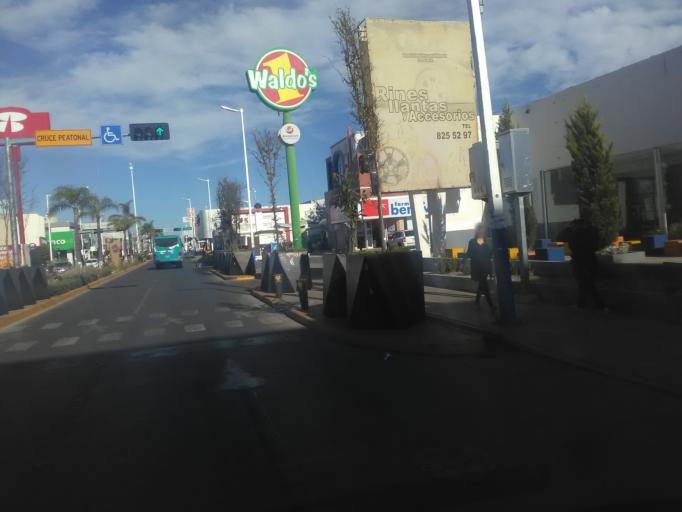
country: MX
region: Durango
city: Victoria de Durango
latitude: 24.0264
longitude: -104.6598
